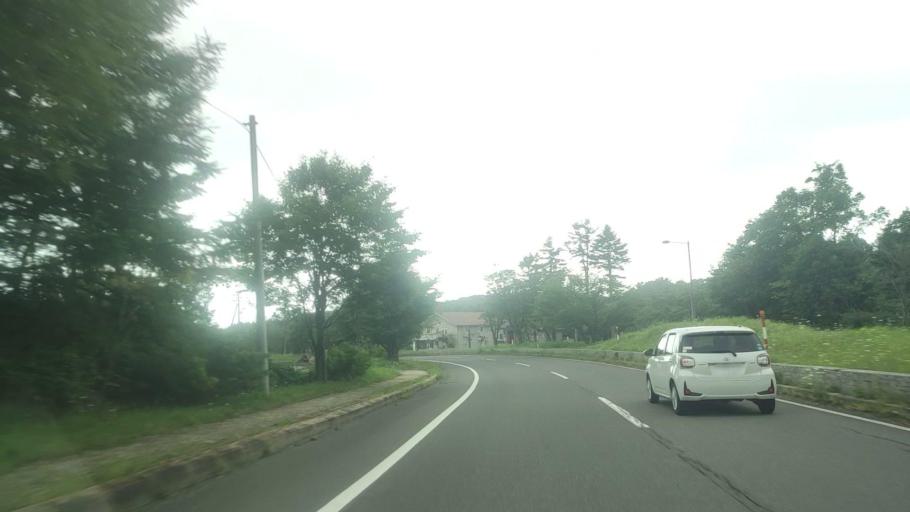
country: JP
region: Hokkaido
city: Shiraoi
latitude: 42.4701
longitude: 141.1600
